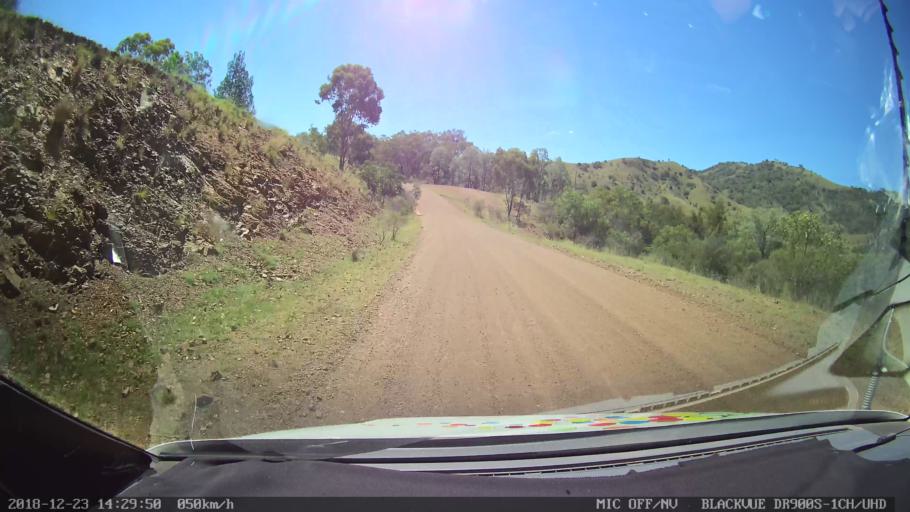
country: AU
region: New South Wales
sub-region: Tamworth Municipality
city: Manilla
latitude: -30.6058
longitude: 150.9360
